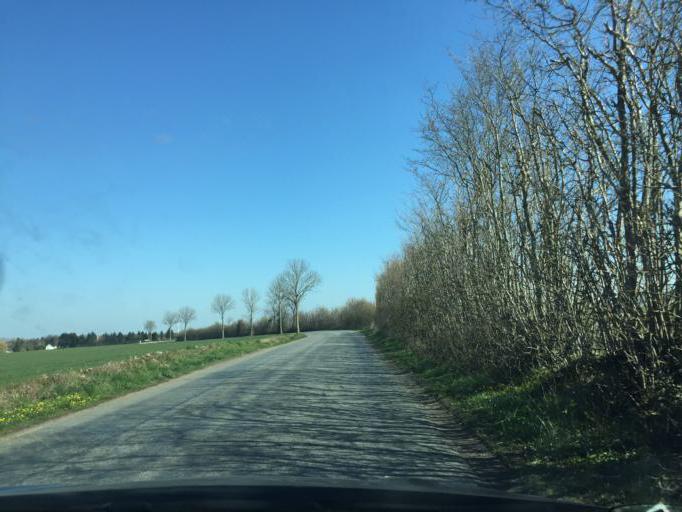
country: DK
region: South Denmark
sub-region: Faaborg-Midtfyn Kommune
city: Ringe
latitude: 55.2712
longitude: 10.5314
